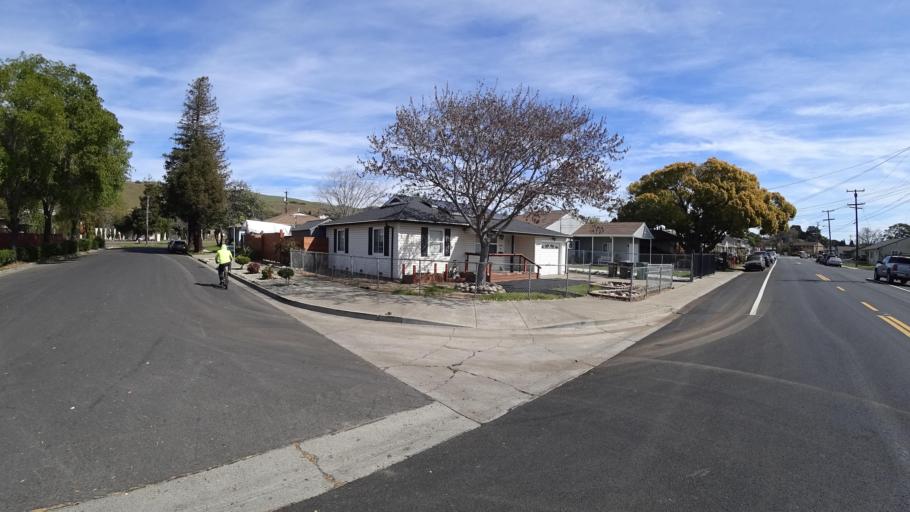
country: US
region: California
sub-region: Alameda County
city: Union City
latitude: 37.6099
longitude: -122.0257
